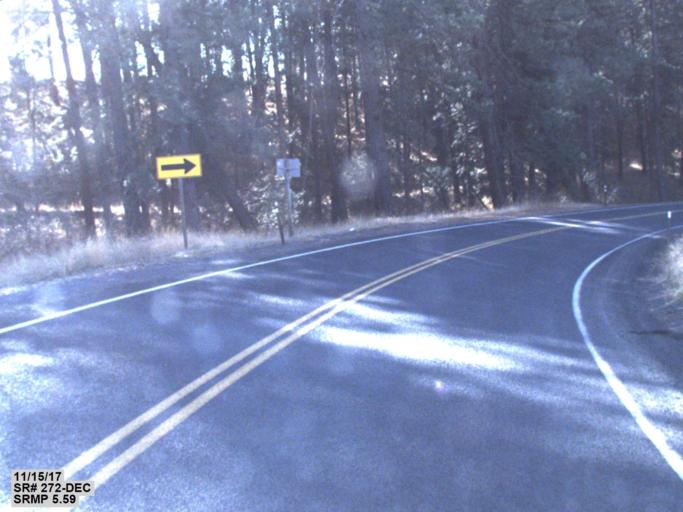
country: US
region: Washington
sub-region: Whitman County
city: Colfax
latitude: 46.9136
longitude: -117.2665
